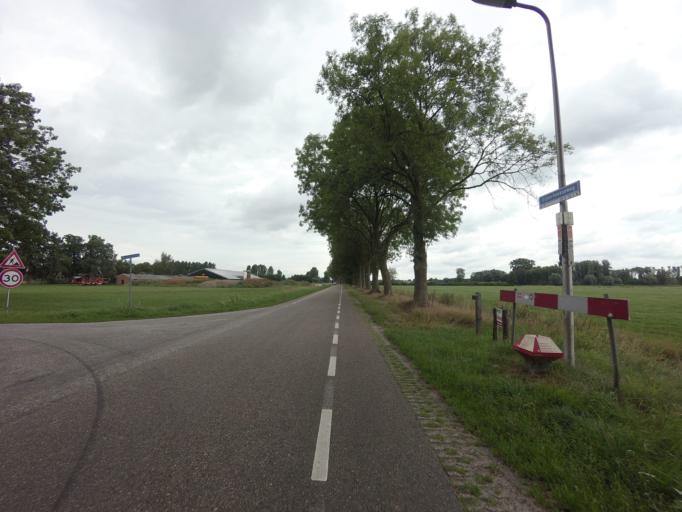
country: NL
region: Gelderland
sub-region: Gemeente Lochem
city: Laren
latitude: 52.2827
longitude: 6.3505
